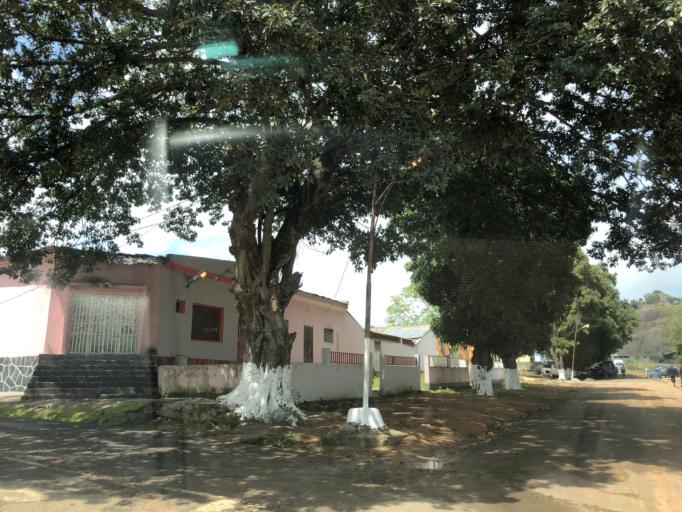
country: AO
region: Cuanza Sul
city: Quibala
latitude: -10.7333
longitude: 14.9791
